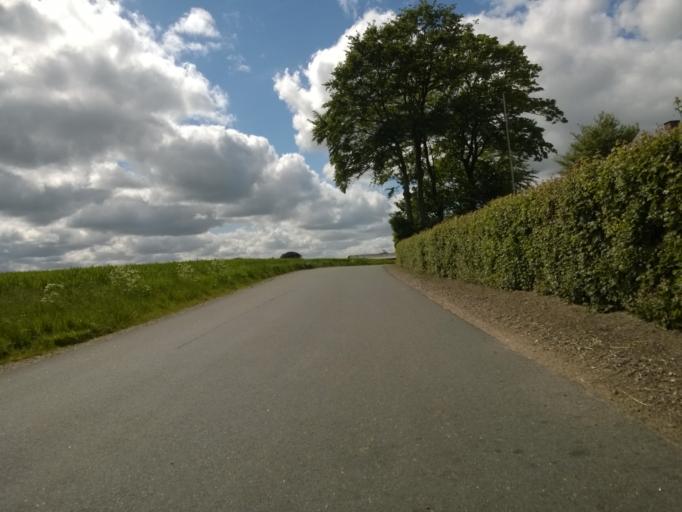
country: DK
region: Central Jutland
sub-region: Holstebro Kommune
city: Vinderup
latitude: 56.4055
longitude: 8.7944
